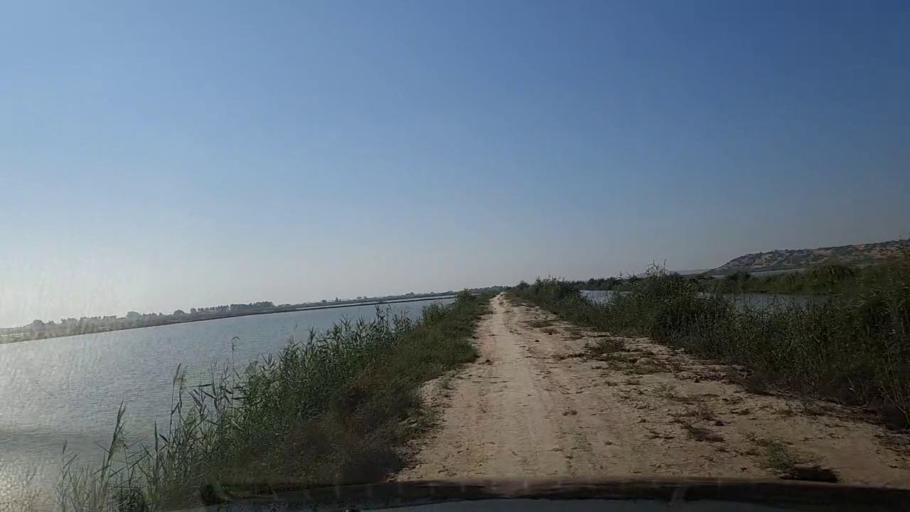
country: PK
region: Sindh
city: Thatta
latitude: 24.6808
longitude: 67.8907
